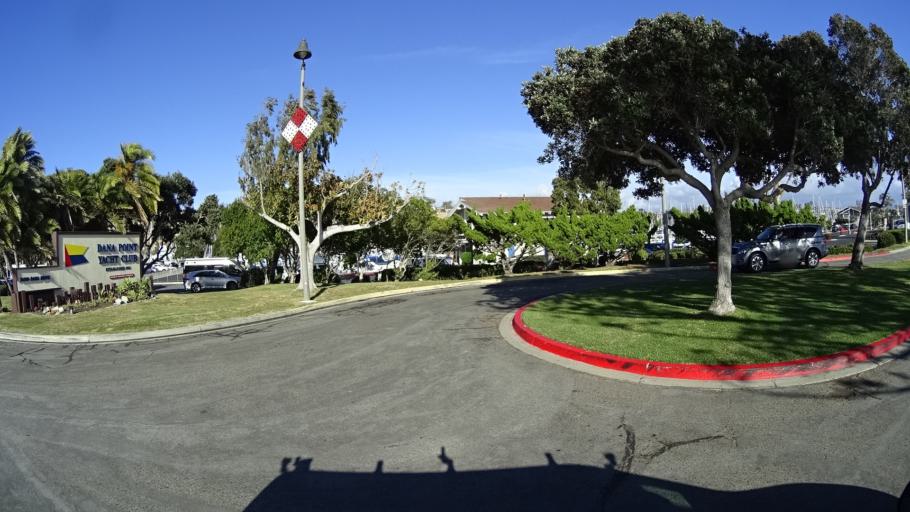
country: US
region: California
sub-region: Orange County
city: Dana Point
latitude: 33.4593
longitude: -117.7039
